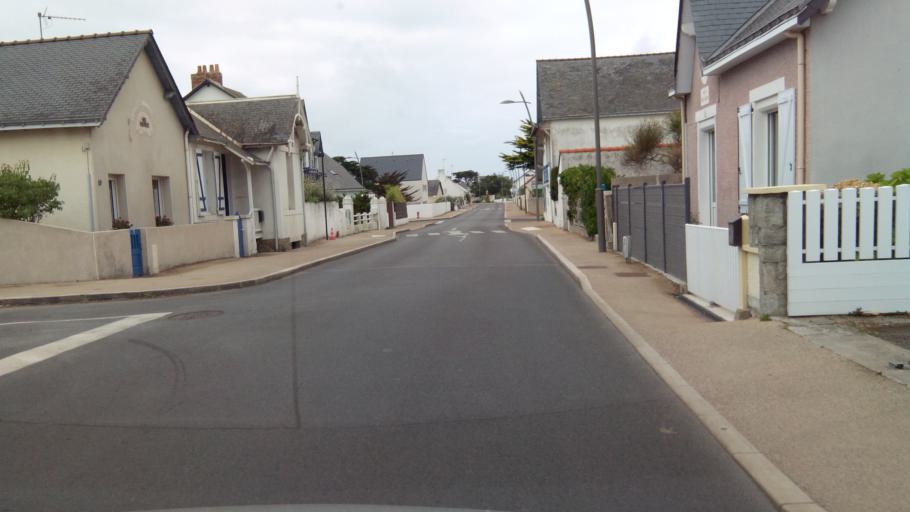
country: FR
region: Pays de la Loire
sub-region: Departement de la Loire-Atlantique
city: Batz-sur-Mer
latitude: 47.2758
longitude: -2.4853
